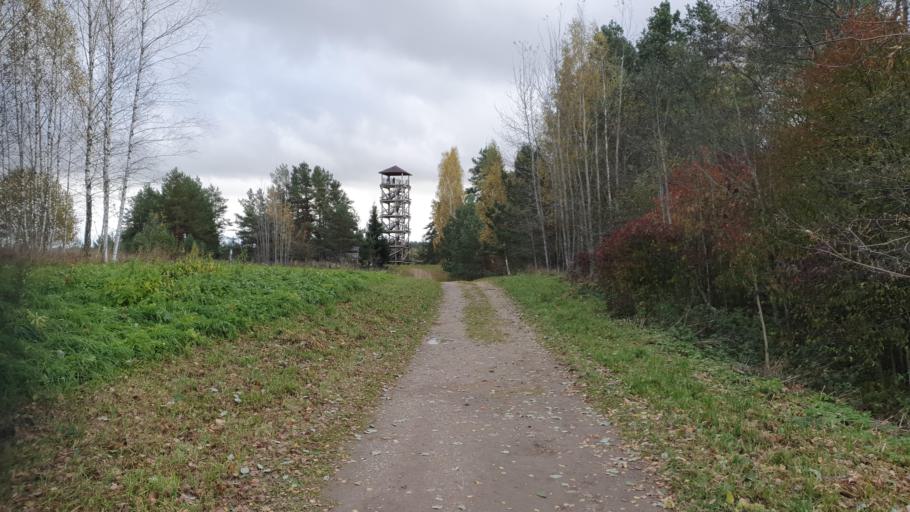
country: LV
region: Daugavpils
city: Daugavpils
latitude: 55.9162
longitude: 26.8148
